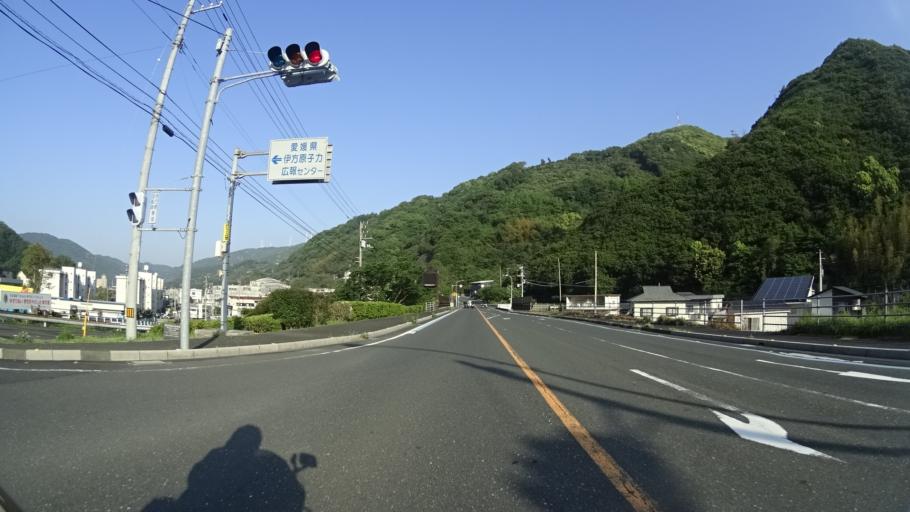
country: JP
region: Ehime
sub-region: Nishiuwa-gun
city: Ikata-cho
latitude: 33.4926
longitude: 132.3619
